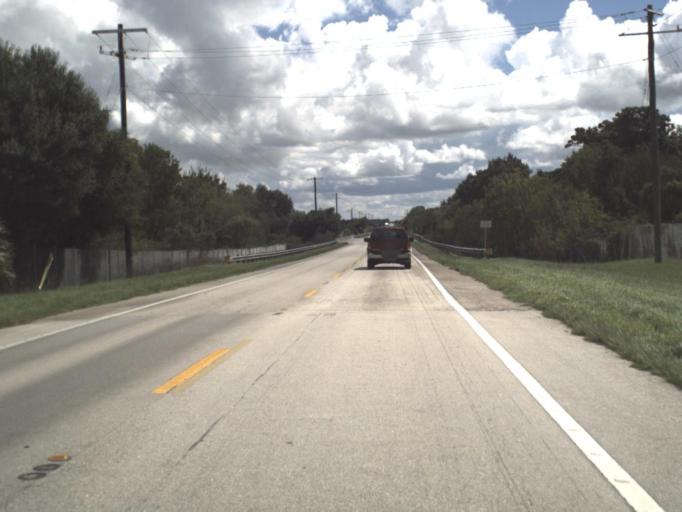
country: US
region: Florida
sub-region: DeSoto County
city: Arcadia
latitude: 27.2616
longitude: -81.9831
